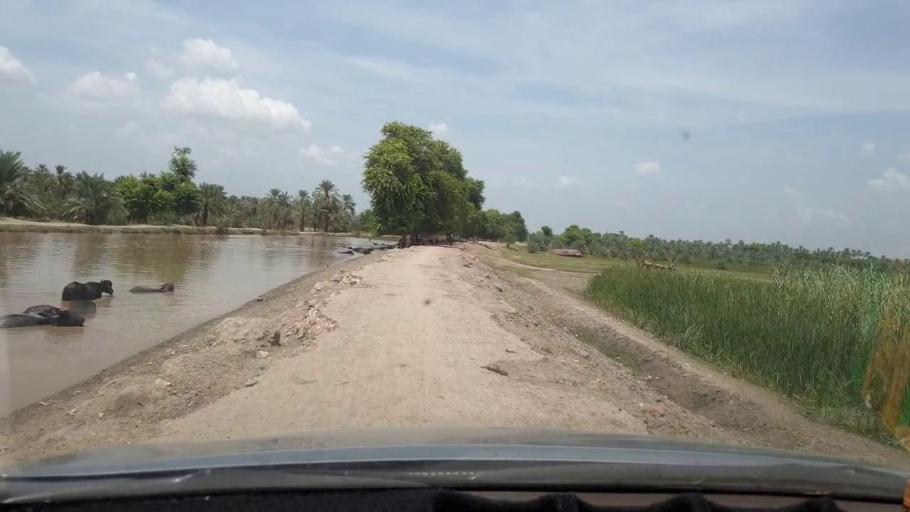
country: PK
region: Sindh
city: Khairpur
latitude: 27.4443
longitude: 68.7962
